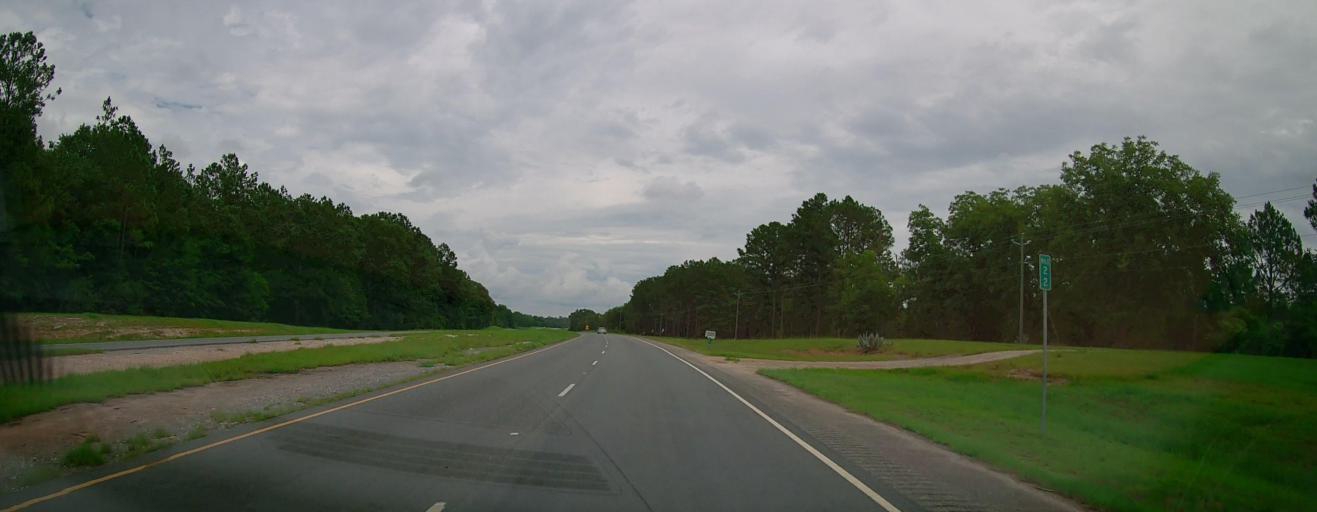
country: US
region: Georgia
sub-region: Telfair County
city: Helena
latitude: 32.1038
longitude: -82.9958
